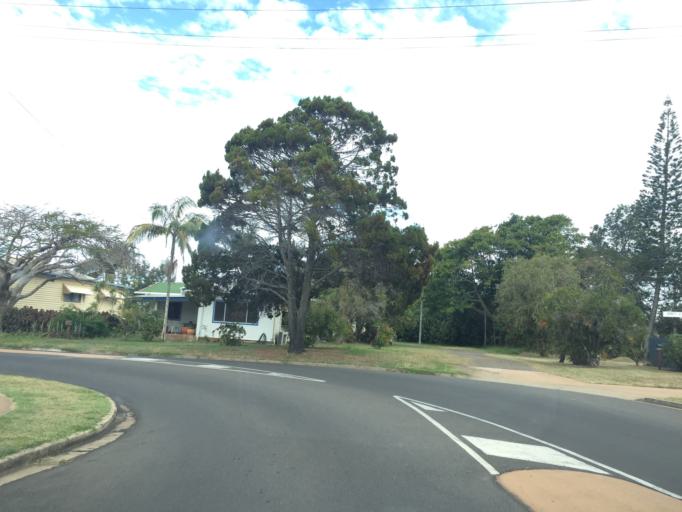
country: AU
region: Queensland
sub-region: Bundaberg
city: Bundaberg
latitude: -24.8163
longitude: 152.4643
